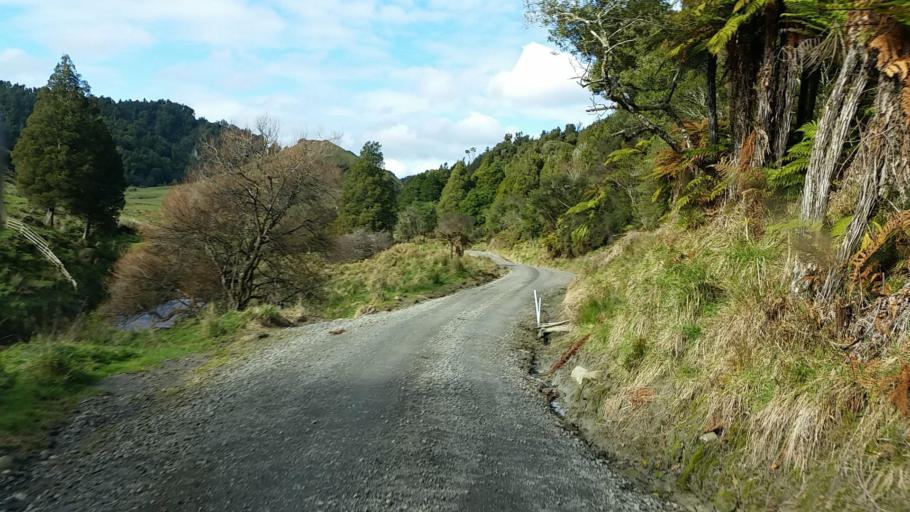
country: NZ
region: Taranaki
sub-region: New Plymouth District
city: Waitara
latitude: -39.0977
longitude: 174.5660
